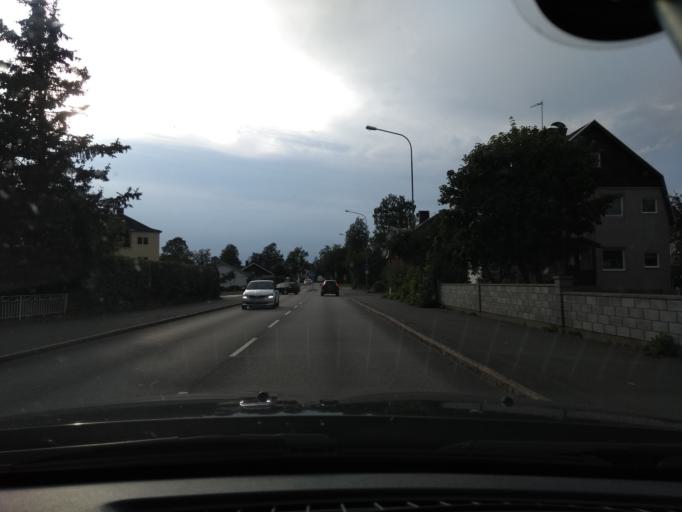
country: SE
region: Joenkoeping
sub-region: Nassjo Kommun
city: Nassjo
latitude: 57.6496
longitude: 14.7139
